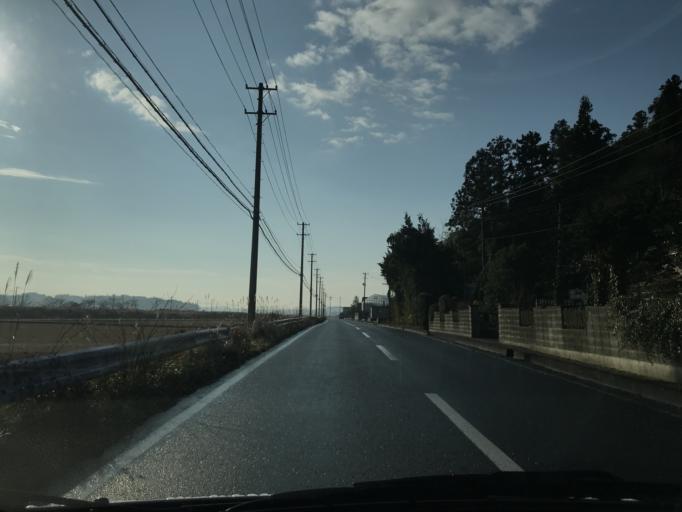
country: JP
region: Iwate
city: Ichinoseki
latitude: 38.8070
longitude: 141.1771
